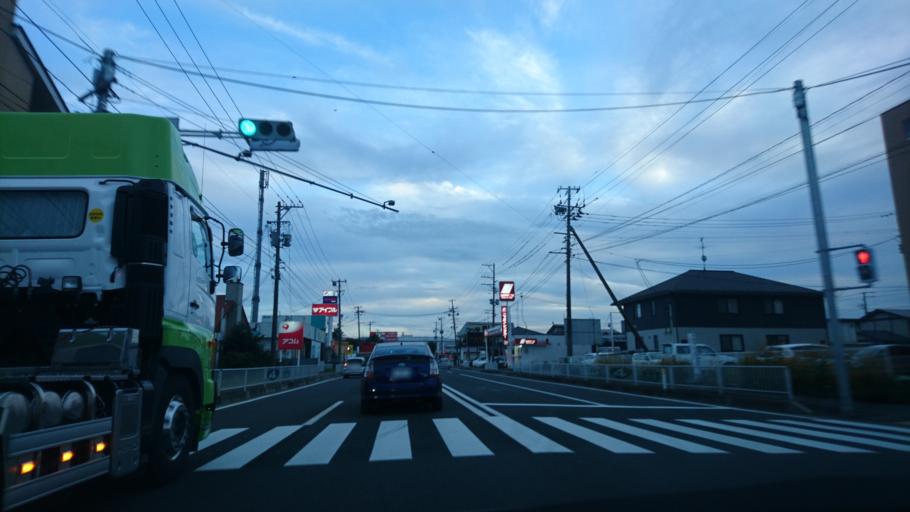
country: JP
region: Iwate
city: Morioka-shi
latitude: 39.6752
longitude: 141.1556
